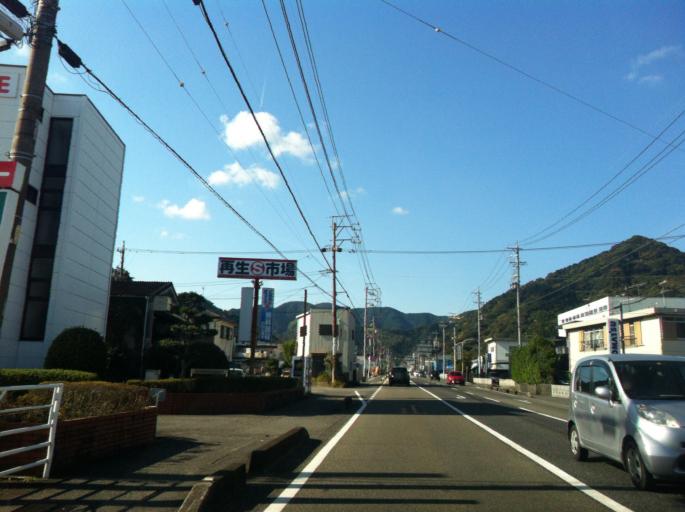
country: JP
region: Shizuoka
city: Shizuoka-shi
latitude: 34.9487
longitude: 138.3500
